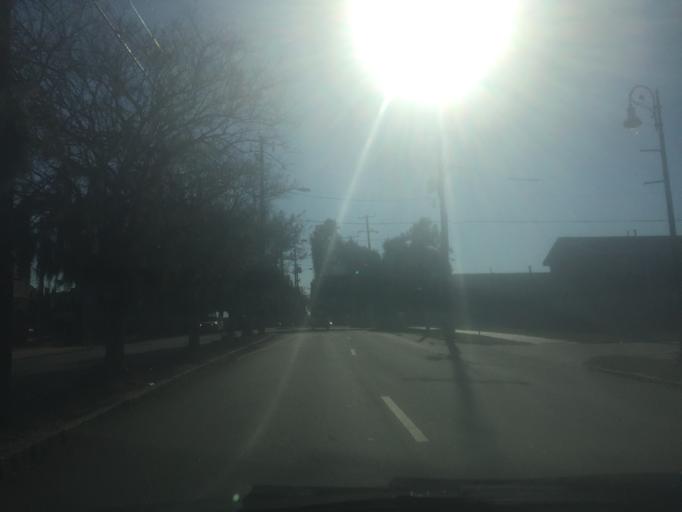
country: US
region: Georgia
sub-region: Chatham County
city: Savannah
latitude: 32.0652
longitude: -81.1030
